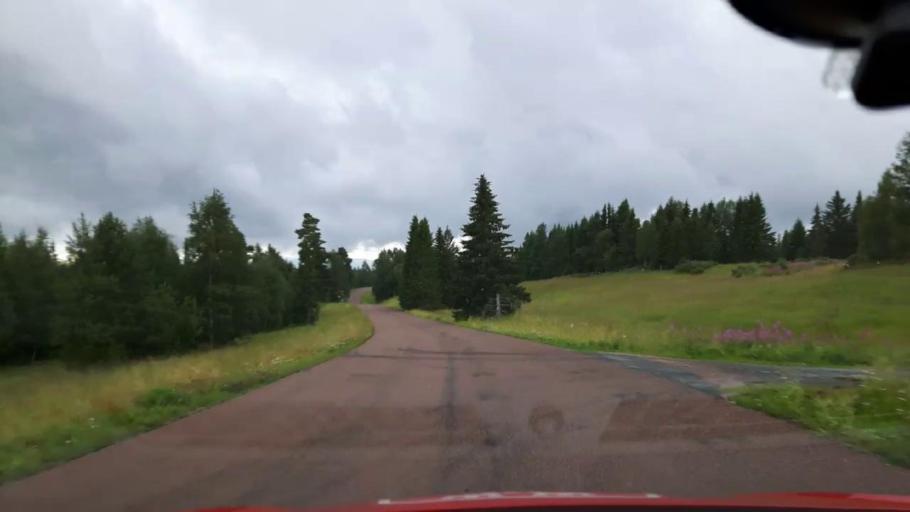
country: SE
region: Jaemtland
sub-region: Krokoms Kommun
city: Valla
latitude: 63.3492
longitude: 13.7223
